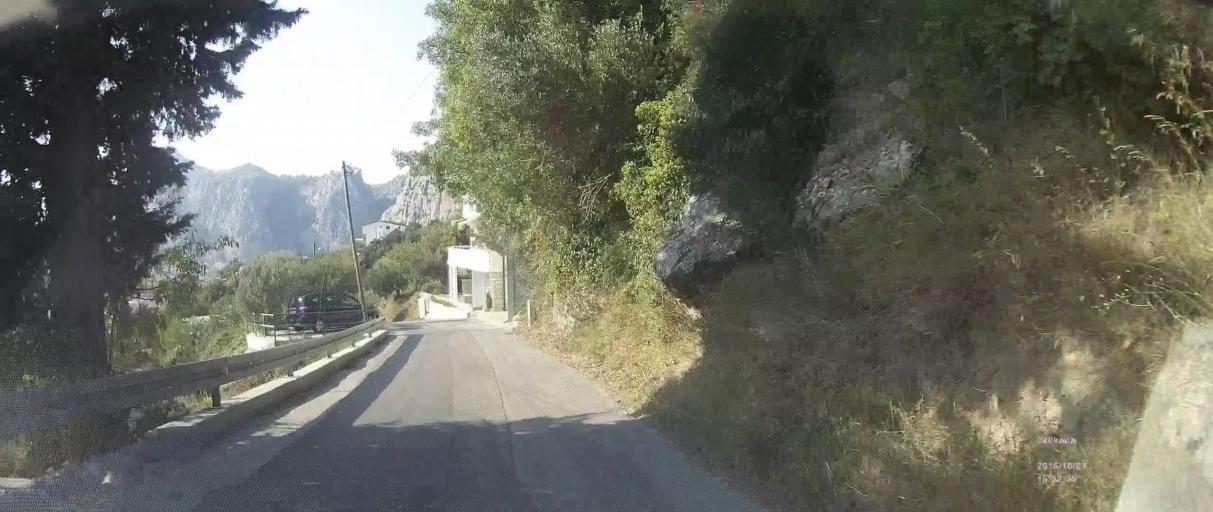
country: HR
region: Splitsko-Dalmatinska
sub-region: Grad Omis
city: Omis
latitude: 43.4382
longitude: 16.7042
